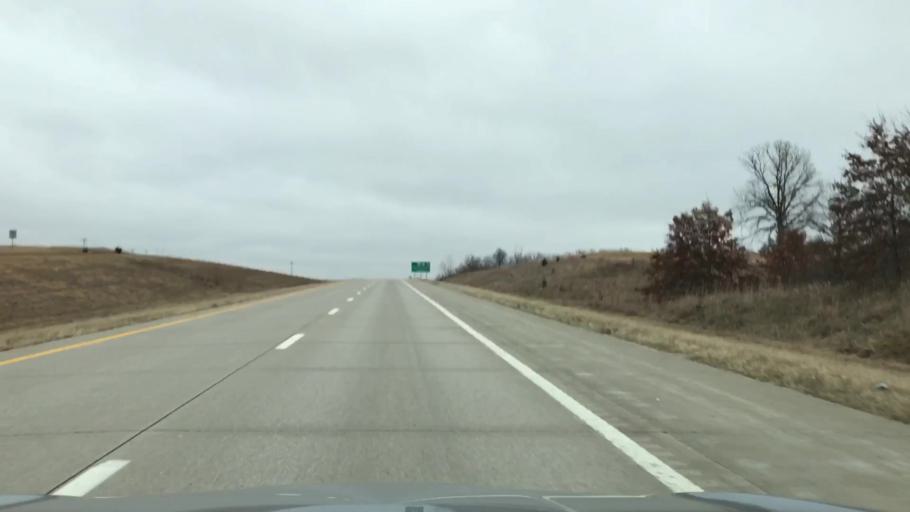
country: US
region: Missouri
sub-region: Linn County
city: Marceline
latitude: 39.7650
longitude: -92.7585
